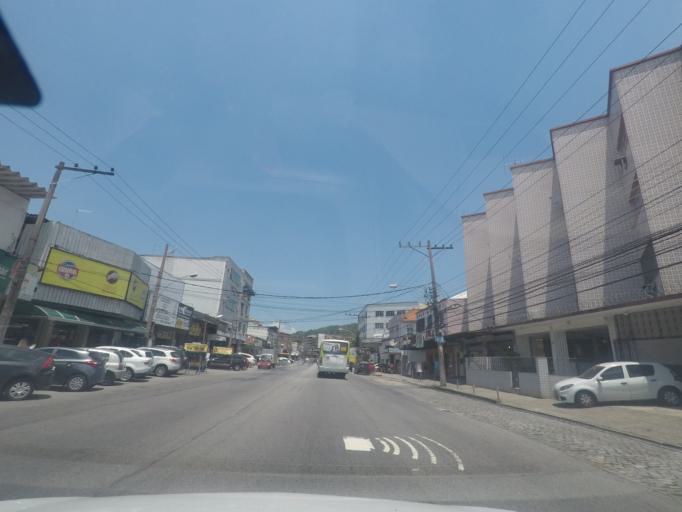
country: BR
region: Rio de Janeiro
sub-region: Duque De Caxias
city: Duque de Caxias
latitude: -22.8404
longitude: -43.3072
